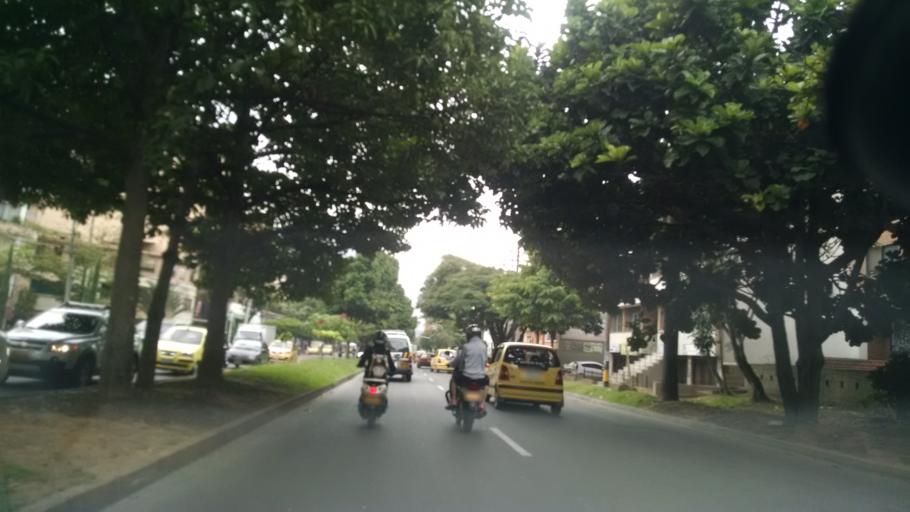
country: CO
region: Antioquia
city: Medellin
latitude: 6.2433
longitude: -75.5937
